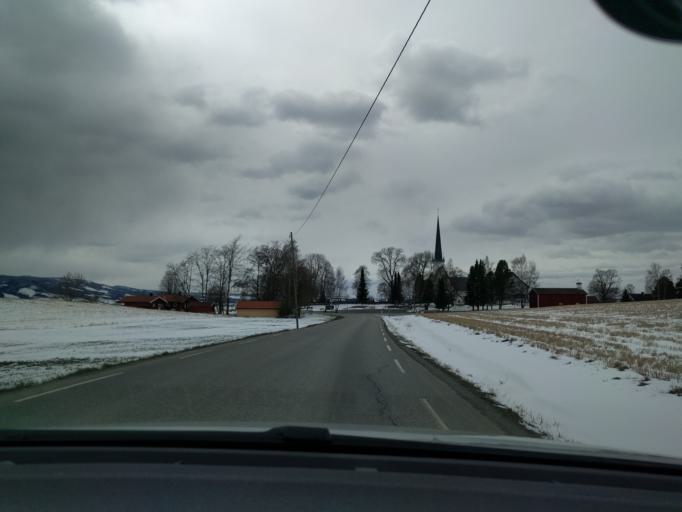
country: NO
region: Hedmark
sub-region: Stange
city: Stange
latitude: 60.7103
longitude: 11.1413
